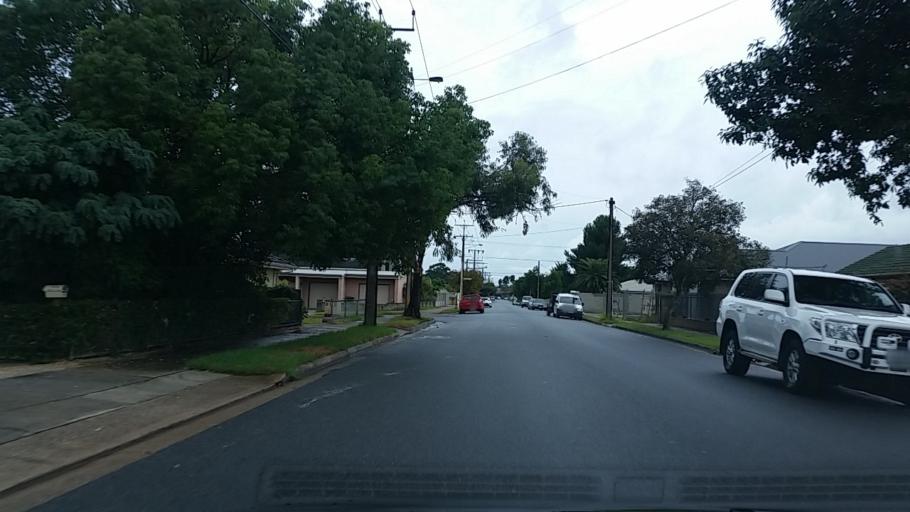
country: AU
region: South Australia
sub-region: Charles Sturt
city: Seaton
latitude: -34.8999
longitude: 138.5202
